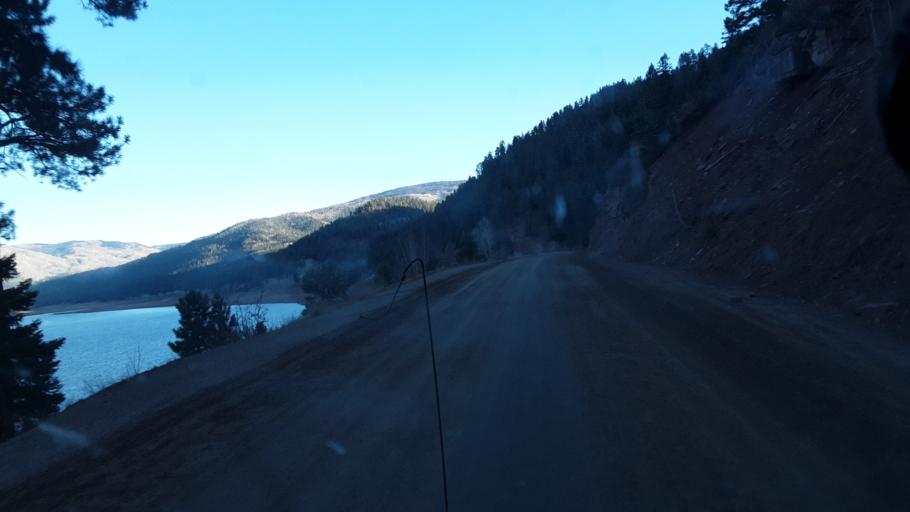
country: US
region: Colorado
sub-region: La Plata County
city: Bayfield
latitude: 37.3819
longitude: -107.6583
